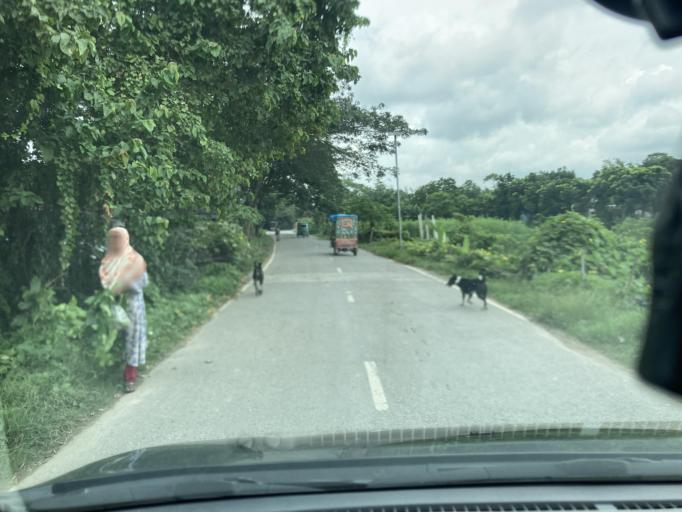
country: BD
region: Dhaka
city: Azimpur
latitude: 23.7857
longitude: 90.2139
